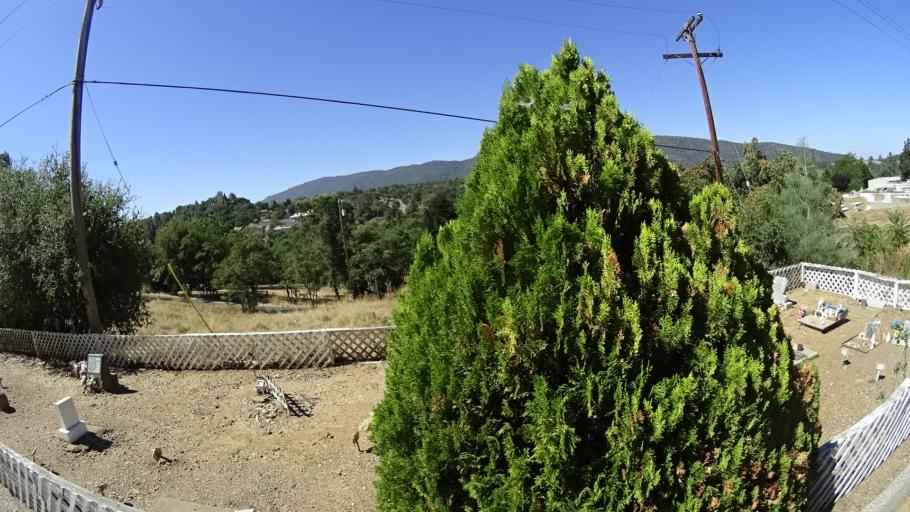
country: US
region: California
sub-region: Calaveras County
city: San Andreas
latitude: 38.1999
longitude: -120.6807
